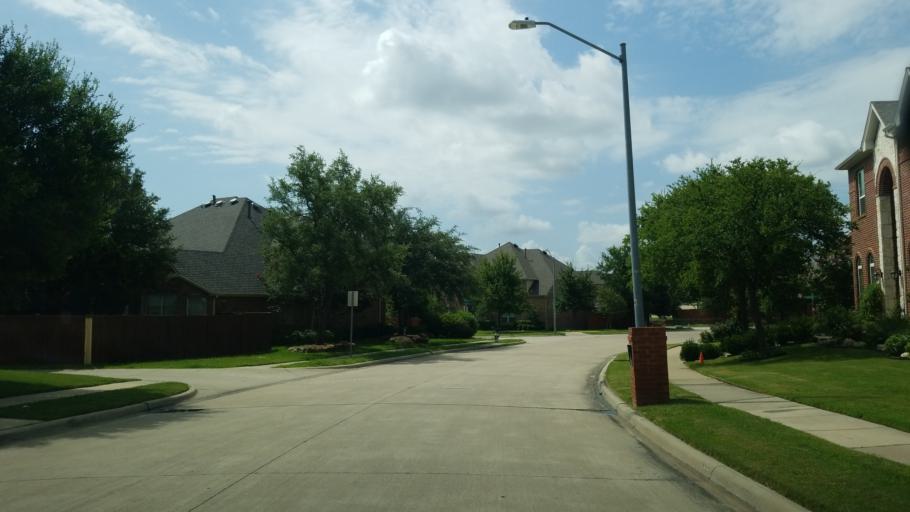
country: US
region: Texas
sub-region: Dallas County
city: Coppell
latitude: 32.9283
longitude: -96.9619
